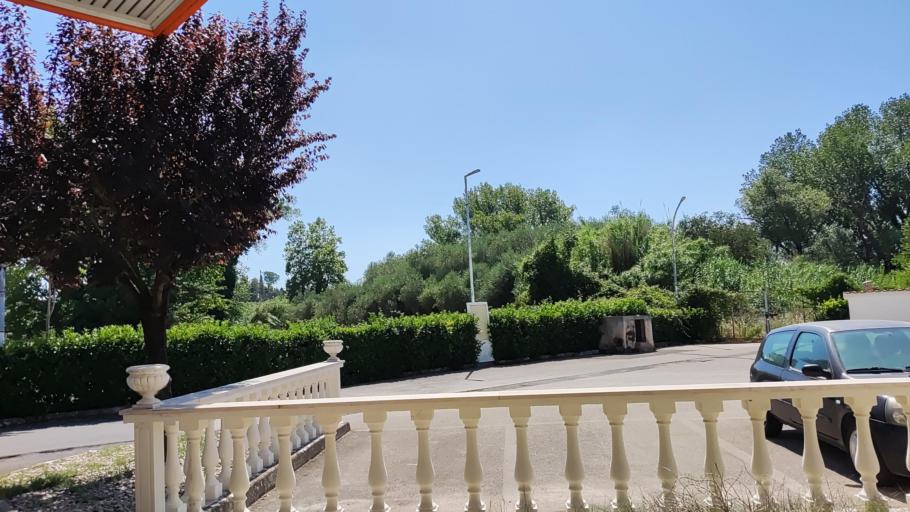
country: IT
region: Latium
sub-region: Citta metropolitana di Roma Capitale
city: Villa Adriana
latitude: 41.9447
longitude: 12.7592
